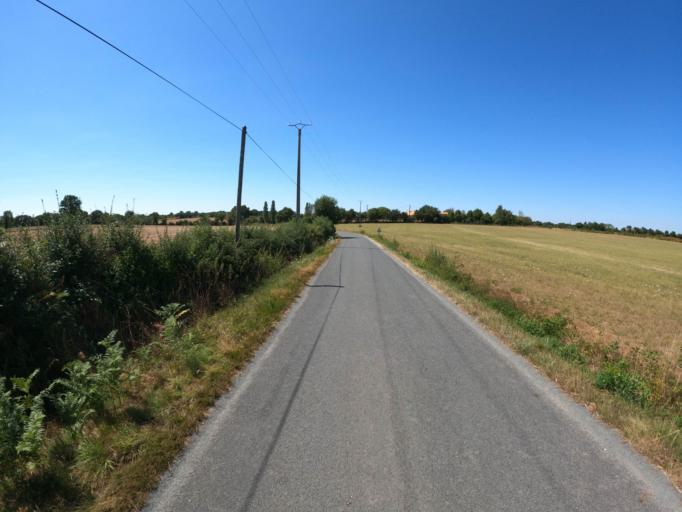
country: FR
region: Pays de la Loire
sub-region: Departement de Maine-et-Loire
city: Saint-Christophe-du-Bois
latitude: 47.0475
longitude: -0.9600
